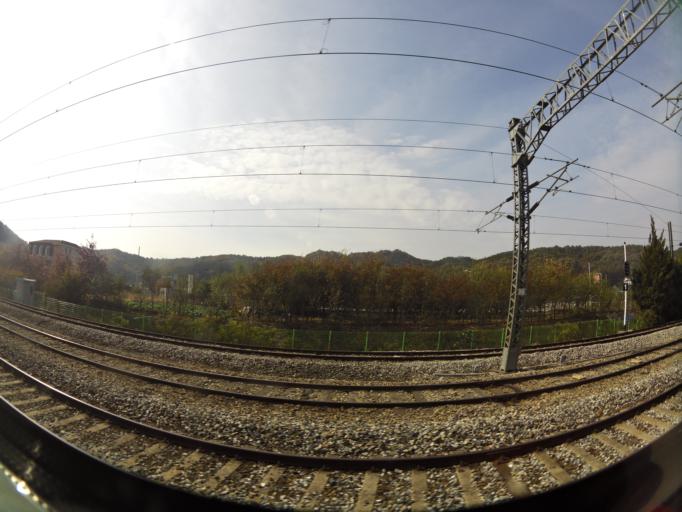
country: KR
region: Chungcheongbuk-do
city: Cheongju-si
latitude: 36.6294
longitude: 127.2898
